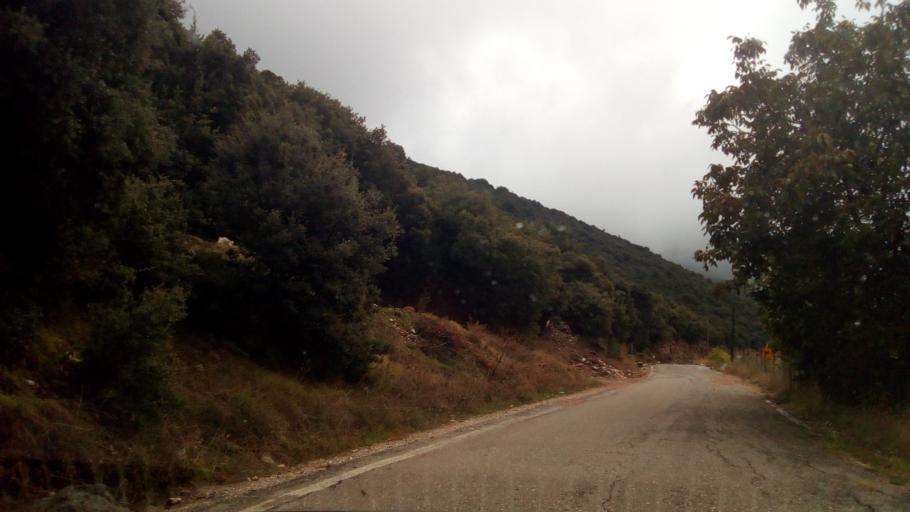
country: GR
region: West Greece
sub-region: Nomos Aitolias kai Akarnanias
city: Nafpaktos
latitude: 38.5249
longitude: 21.8362
